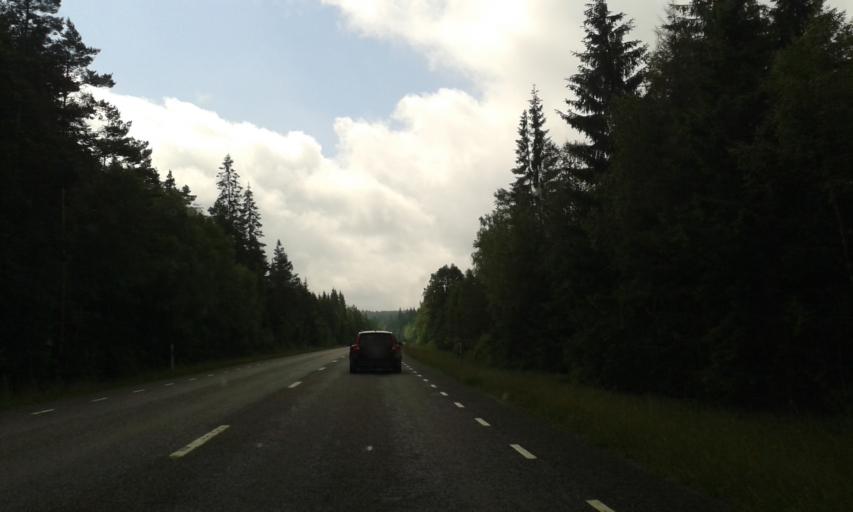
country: SE
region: Vaestra Goetaland
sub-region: Tranemo Kommun
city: Tranemo
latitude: 57.4142
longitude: 13.4530
